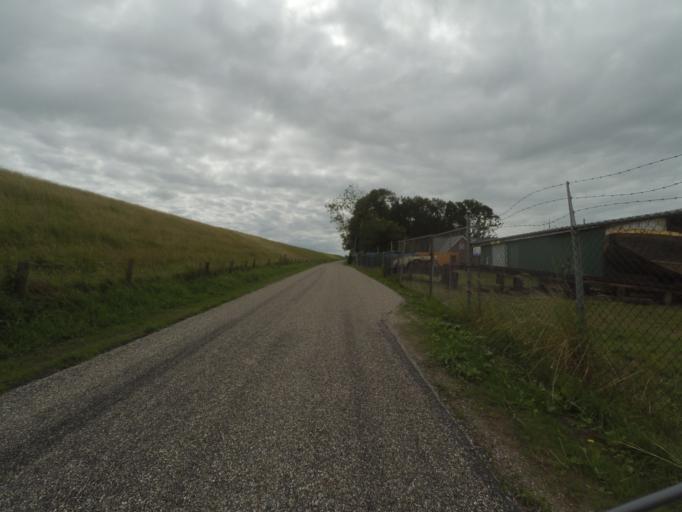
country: NL
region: Friesland
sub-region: Gemeente Dongeradeel
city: Anjum
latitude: 53.3574
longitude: 6.1467
